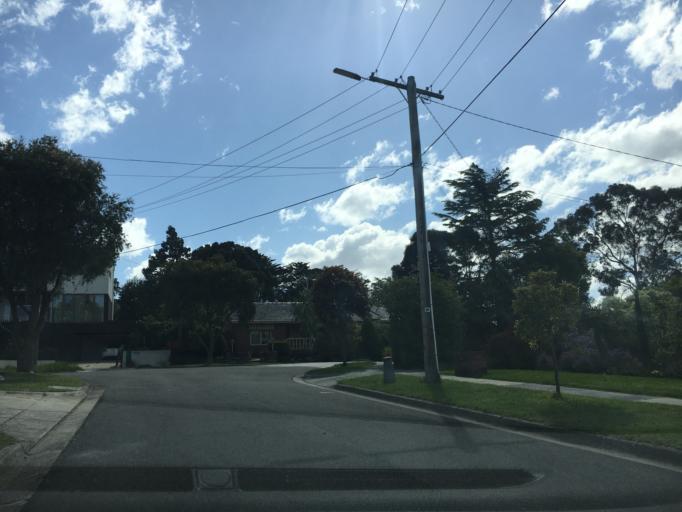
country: AU
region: Victoria
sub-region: Monash
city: Mulgrave
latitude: -37.8920
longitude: 145.1836
